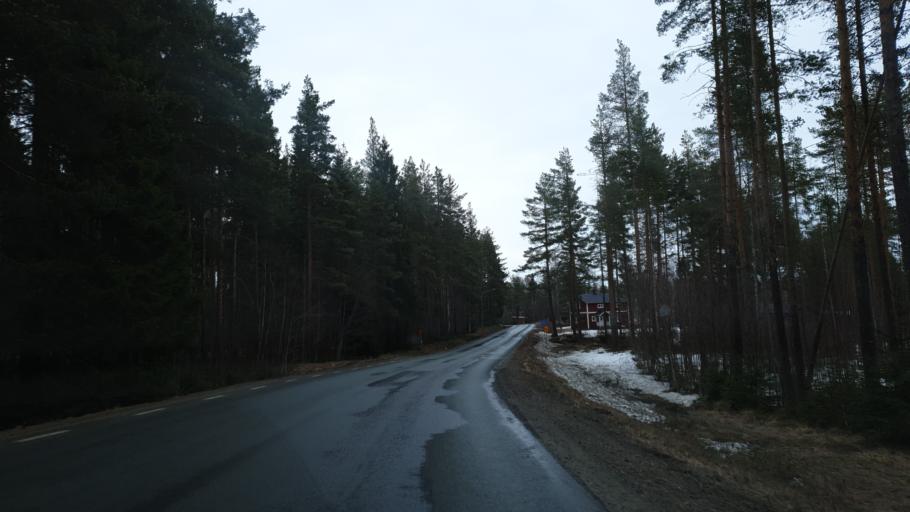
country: SE
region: Vaesterbotten
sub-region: Skelleftea Kommun
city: Kage
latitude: 64.8255
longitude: 20.9830
